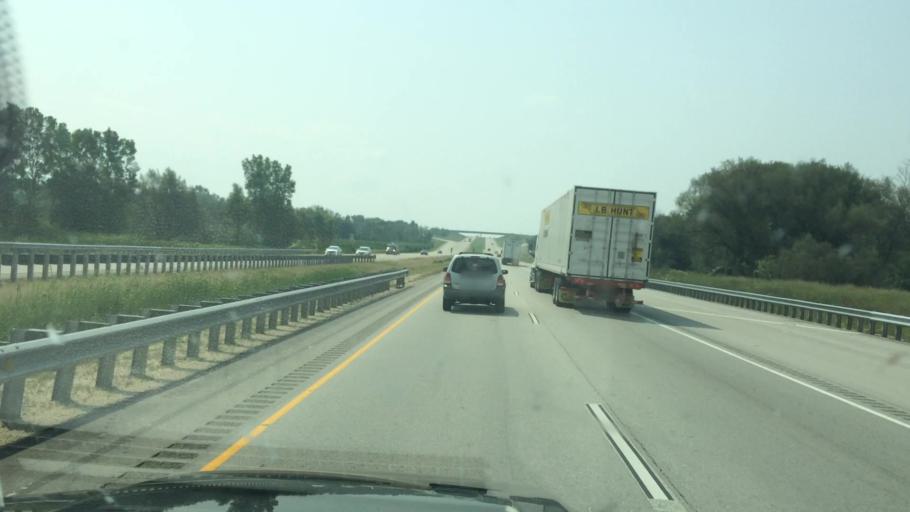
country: US
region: Wisconsin
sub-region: Dodge County
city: Theresa
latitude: 43.4835
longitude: -88.3670
